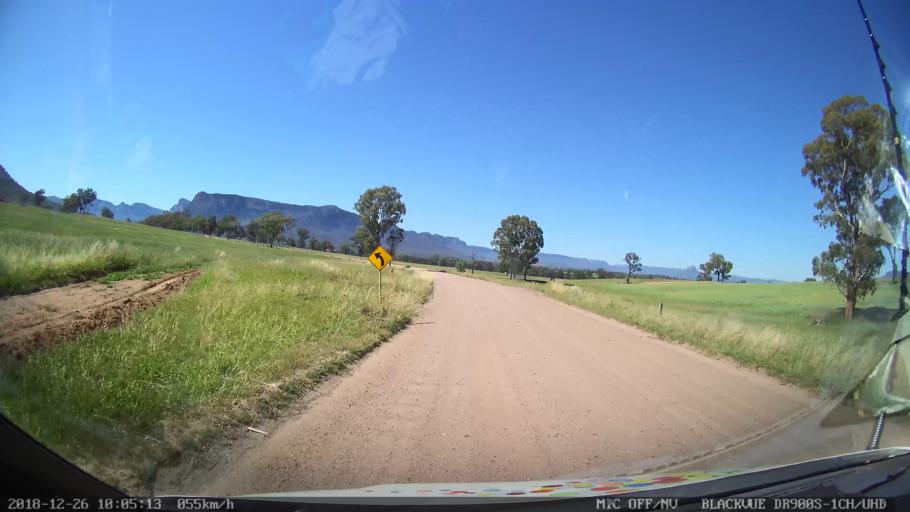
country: AU
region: New South Wales
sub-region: Mid-Western Regional
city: Kandos
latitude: -33.0764
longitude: 150.2120
